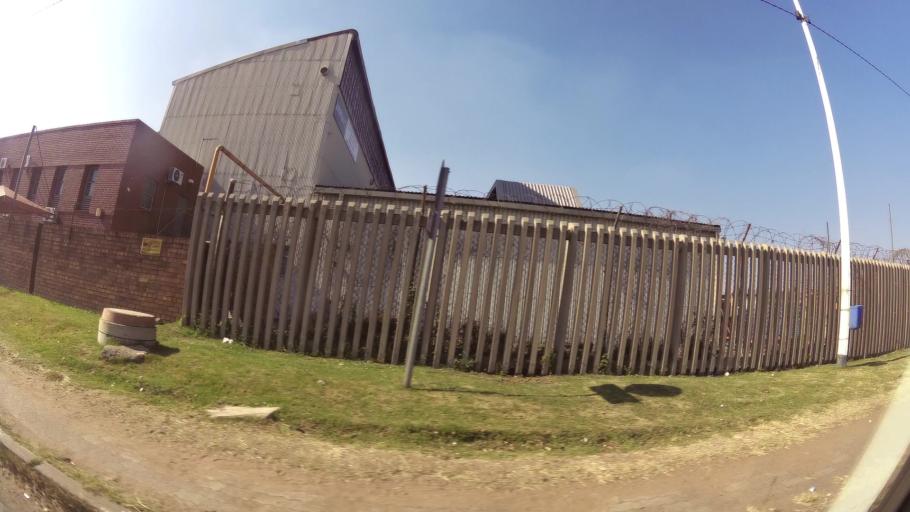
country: ZA
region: Gauteng
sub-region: Ekurhuleni Metropolitan Municipality
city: Boksburg
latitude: -26.2148
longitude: 28.2875
